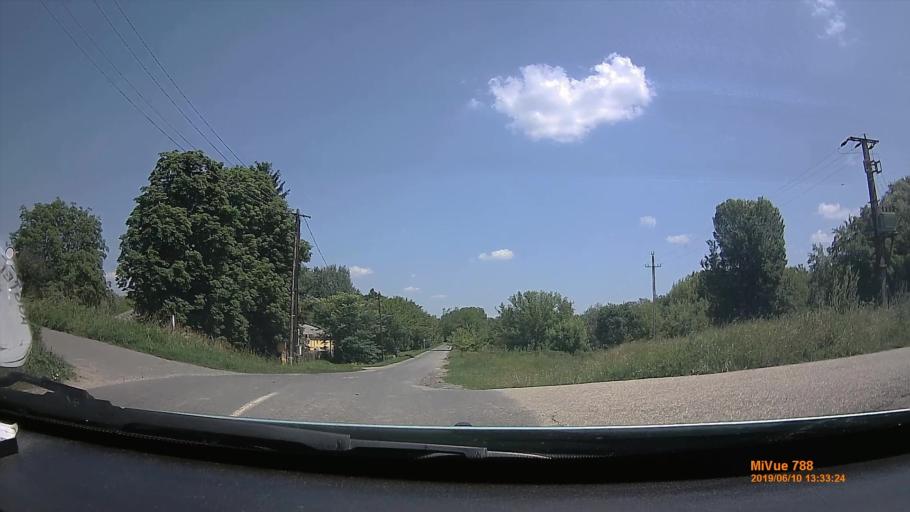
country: HU
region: Szabolcs-Szatmar-Bereg
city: Tiszadob
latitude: 48.0110
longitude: 21.1489
